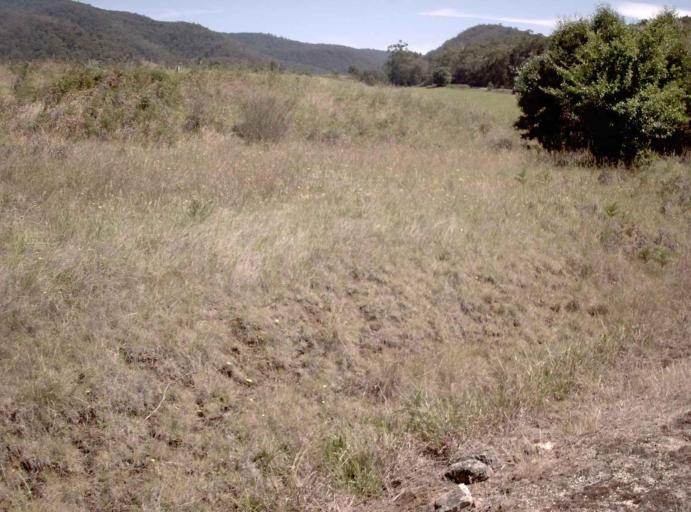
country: AU
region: Victoria
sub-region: East Gippsland
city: Lakes Entrance
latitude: -37.3923
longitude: 148.2183
